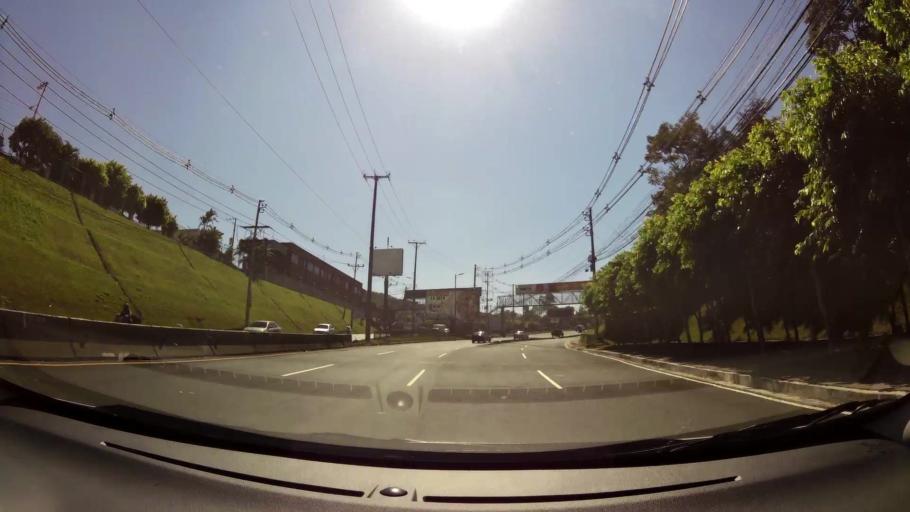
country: SV
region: La Libertad
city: Nuevo Cuscatlan
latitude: 13.6587
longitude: -89.2789
